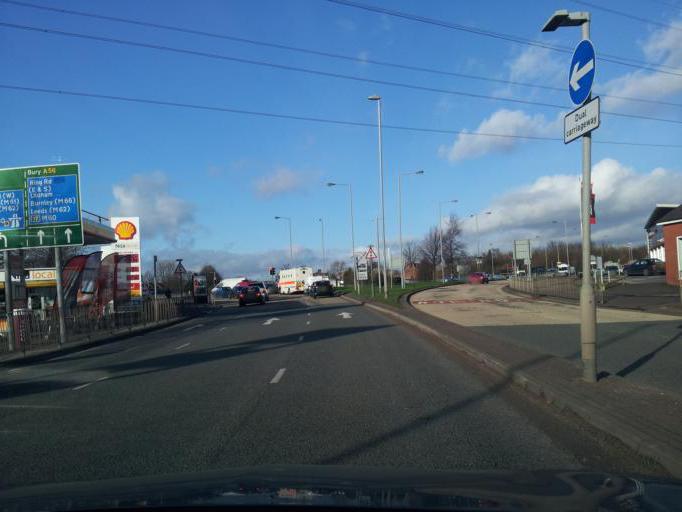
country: GB
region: England
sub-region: Borough of Bury
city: Prestwich
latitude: 53.5374
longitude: -2.2884
